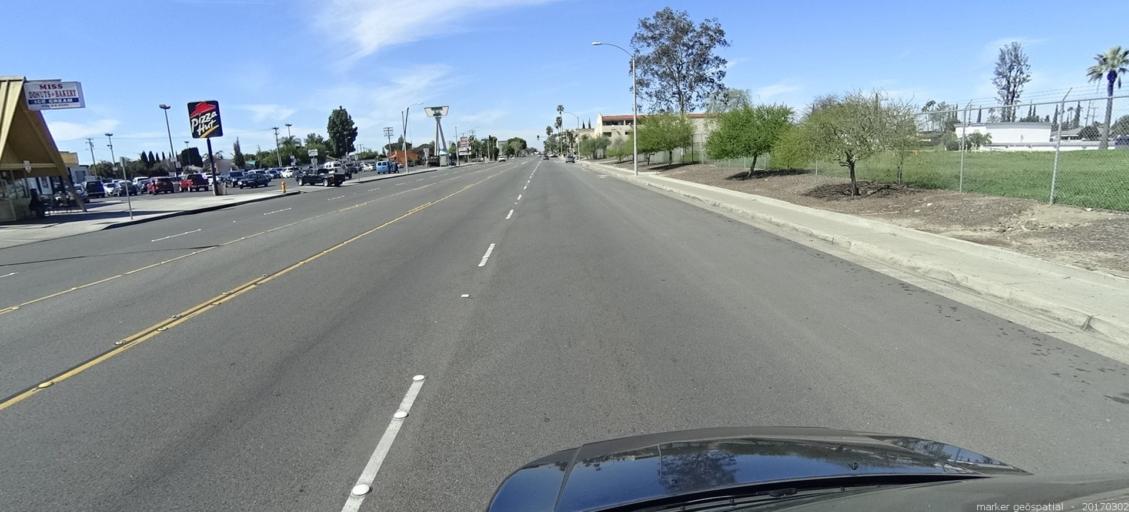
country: US
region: California
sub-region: Orange County
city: Anaheim
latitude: 33.8472
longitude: -117.9260
